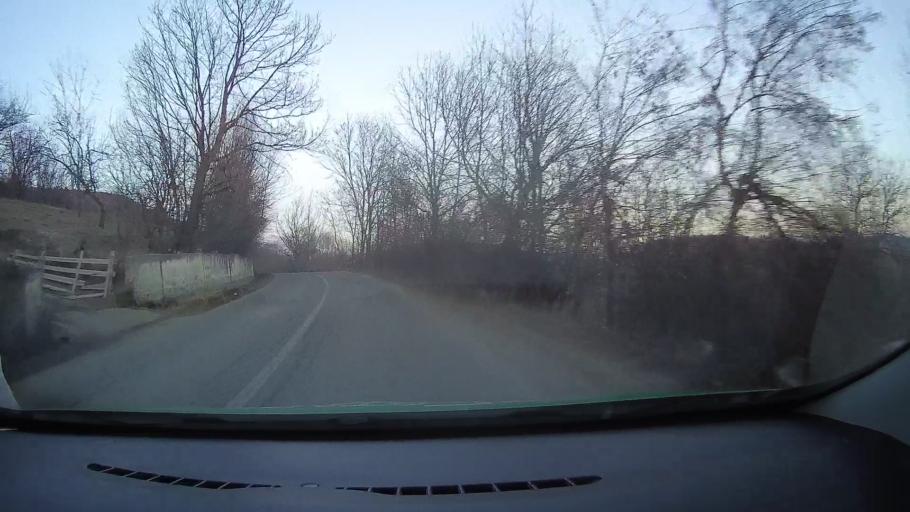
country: RO
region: Prahova
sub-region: Comuna Comarnic
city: Poiana
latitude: 45.2590
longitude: 25.6515
